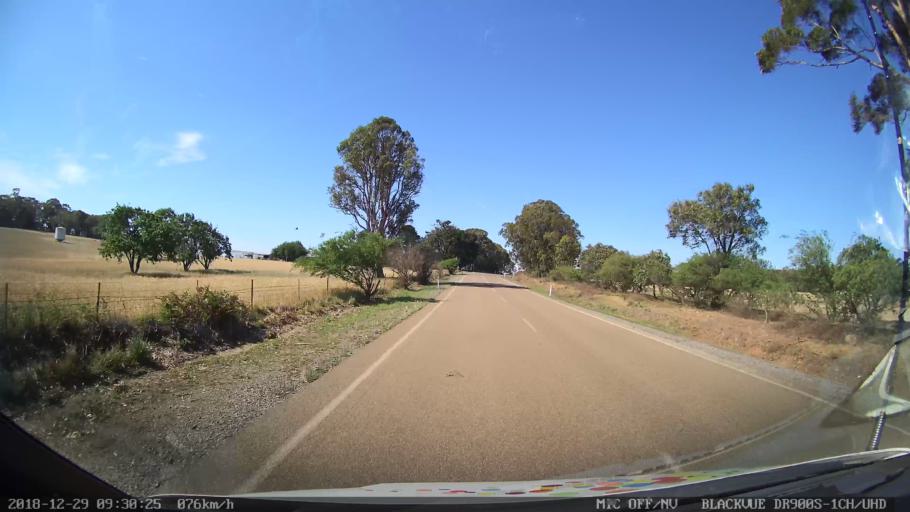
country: AU
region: New South Wales
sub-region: Upper Lachlan Shire
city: Crookwell
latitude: -34.5984
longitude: 149.3692
